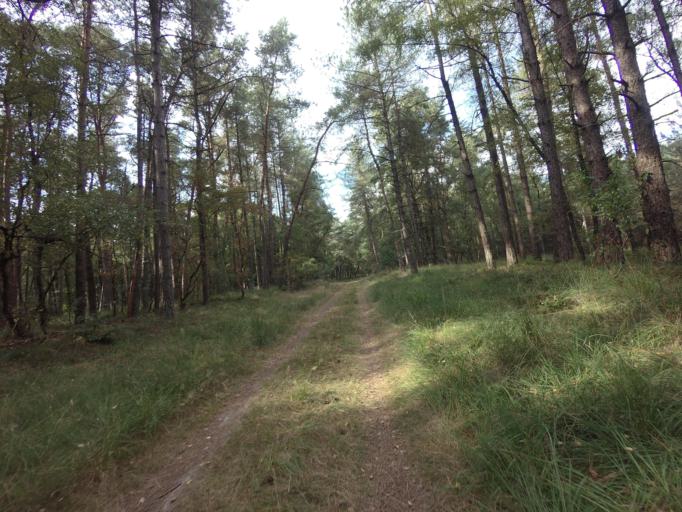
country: NL
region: Gelderland
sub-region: Gemeente Brummen
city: Eerbeek
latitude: 52.0661
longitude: 6.0316
